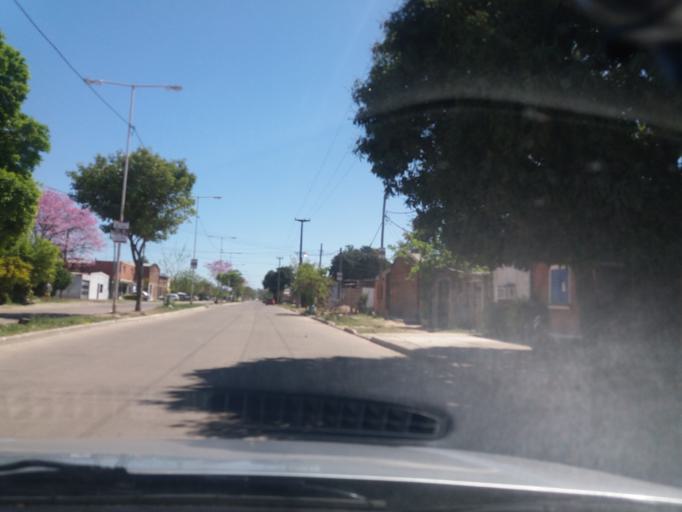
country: AR
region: Corrientes
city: Corrientes
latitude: -27.4890
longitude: -58.8386
